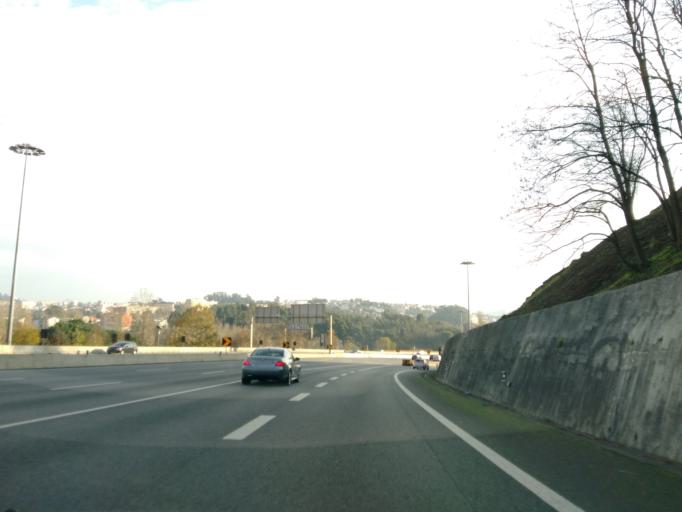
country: PT
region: Porto
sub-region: Gondomar
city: Valbom
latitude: 41.1518
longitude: -8.5801
